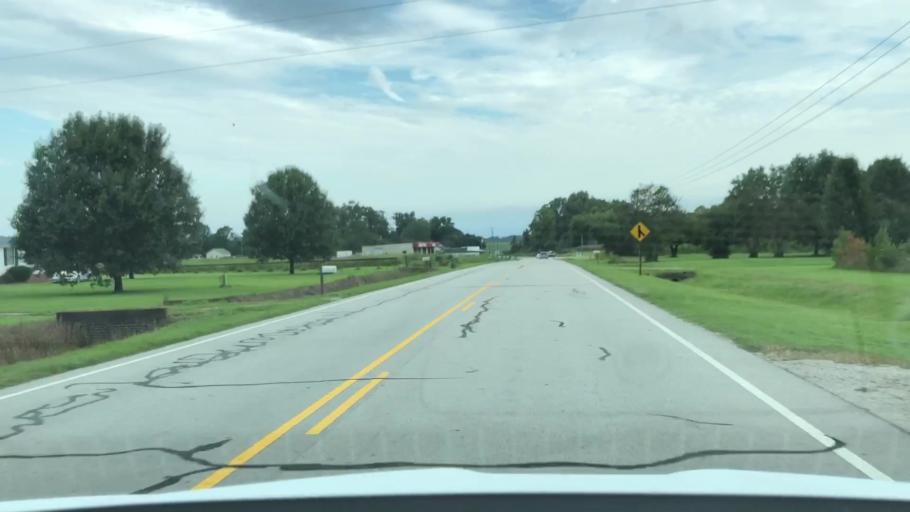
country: US
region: North Carolina
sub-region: Lenoir County
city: Kinston
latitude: 35.1361
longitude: -77.5279
